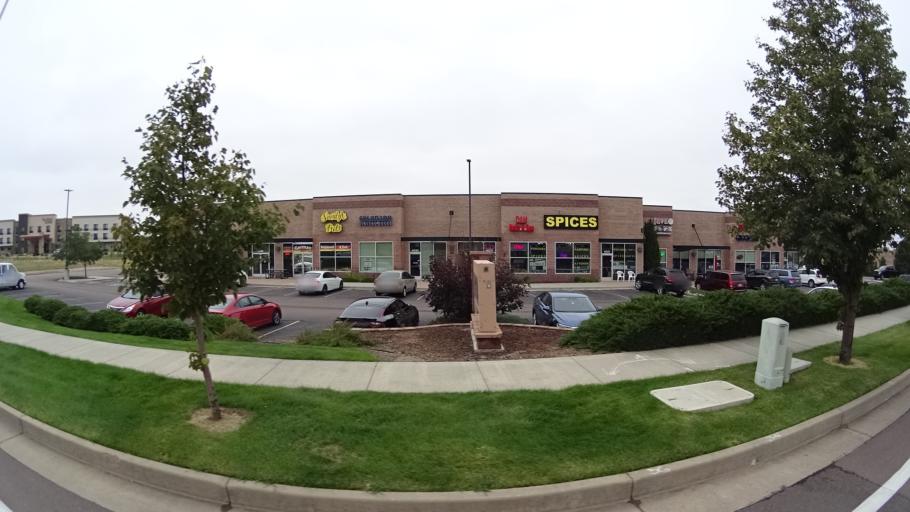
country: US
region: Colorado
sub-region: El Paso County
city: Cimarron Hills
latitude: 38.8900
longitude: -104.7148
